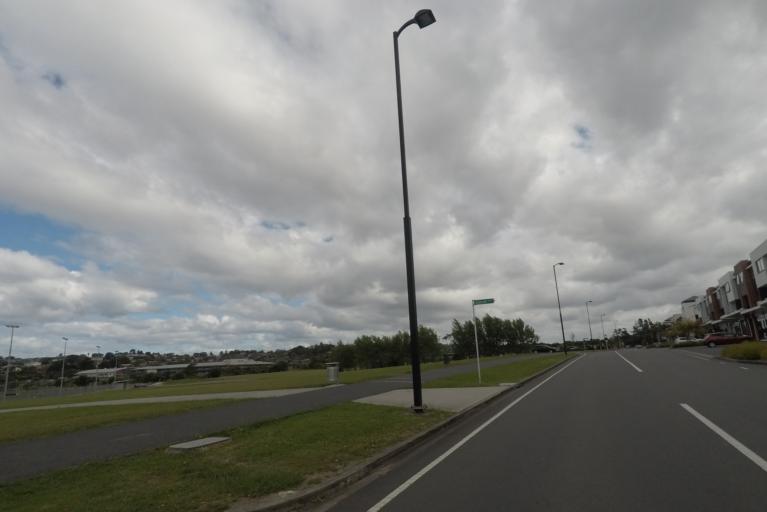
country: NZ
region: Auckland
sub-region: Auckland
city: Rothesay Bay
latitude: -36.6032
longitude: 174.6791
